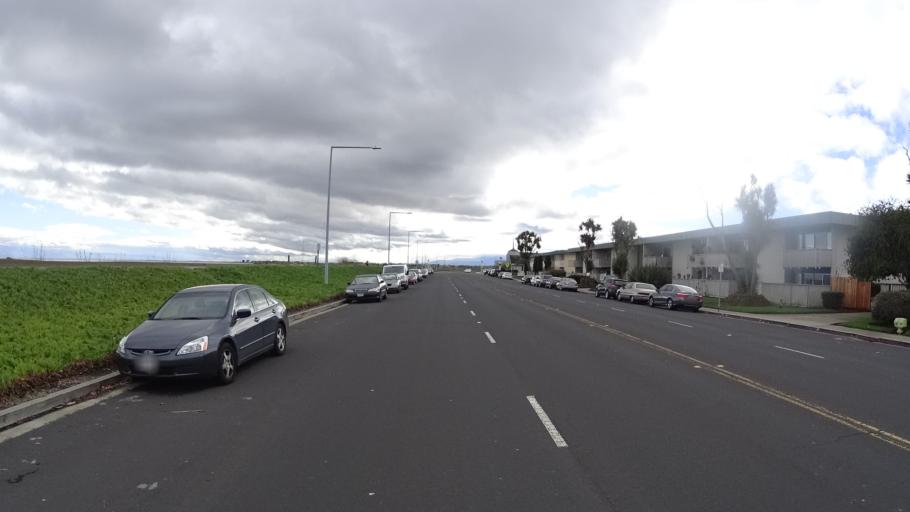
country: US
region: California
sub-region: San Mateo County
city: Foster City
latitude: 37.5625
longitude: -122.2490
